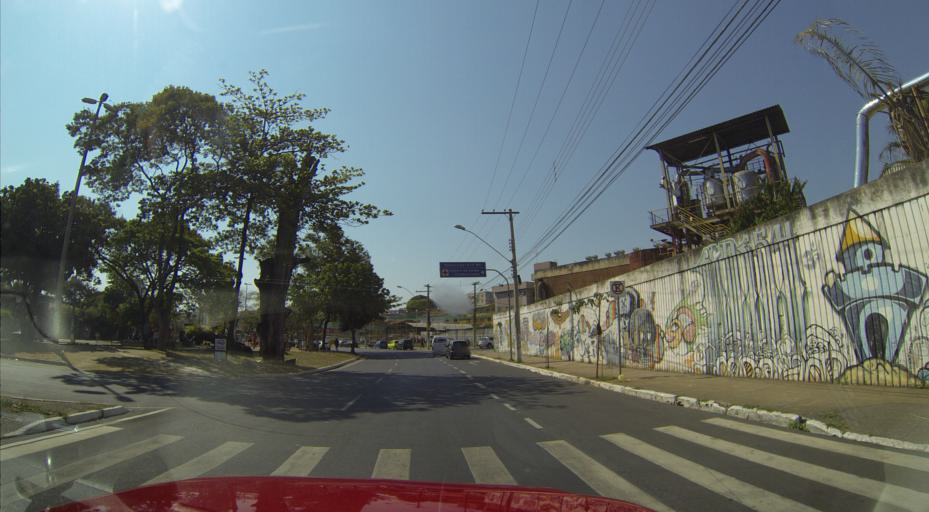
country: BR
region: Minas Gerais
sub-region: Belo Horizonte
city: Belo Horizonte
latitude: -19.8870
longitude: -43.9455
